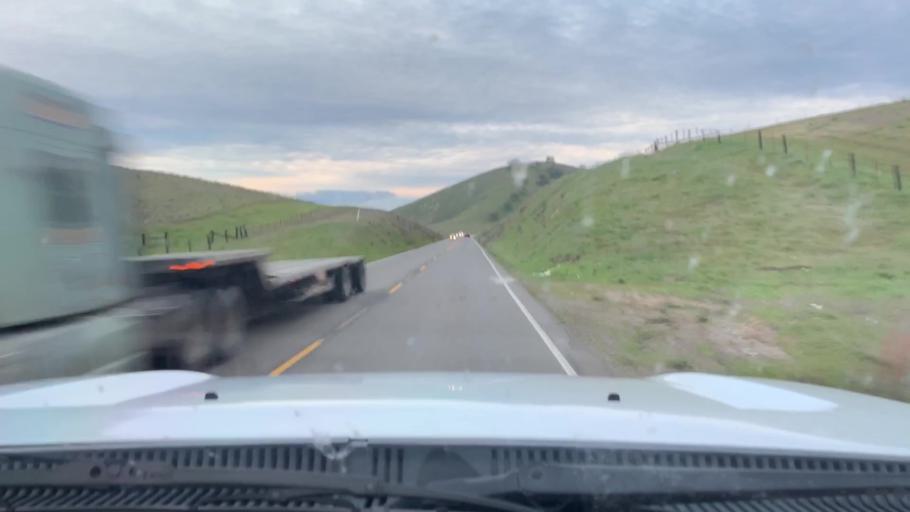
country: US
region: California
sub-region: San Luis Obispo County
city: Shandon
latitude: 35.7752
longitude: -120.2296
